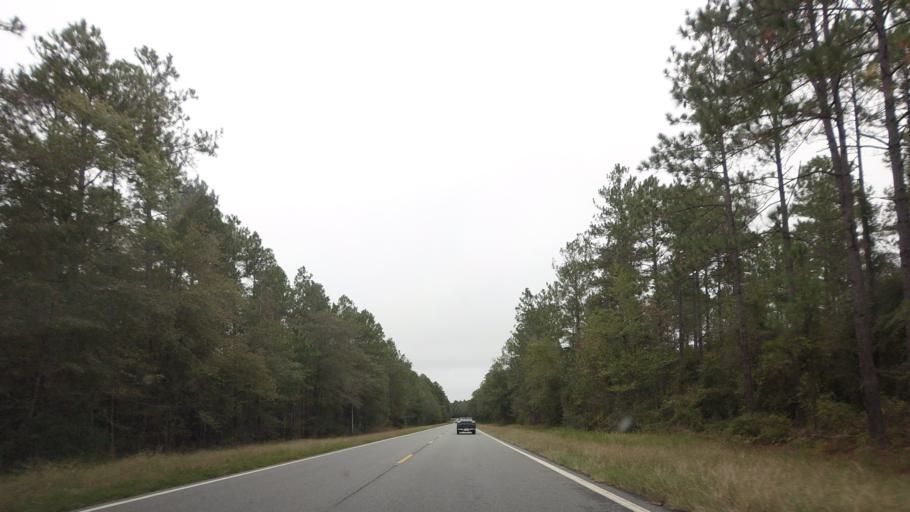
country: US
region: Georgia
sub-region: Berrien County
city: Enigma
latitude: 31.4136
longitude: -83.2428
